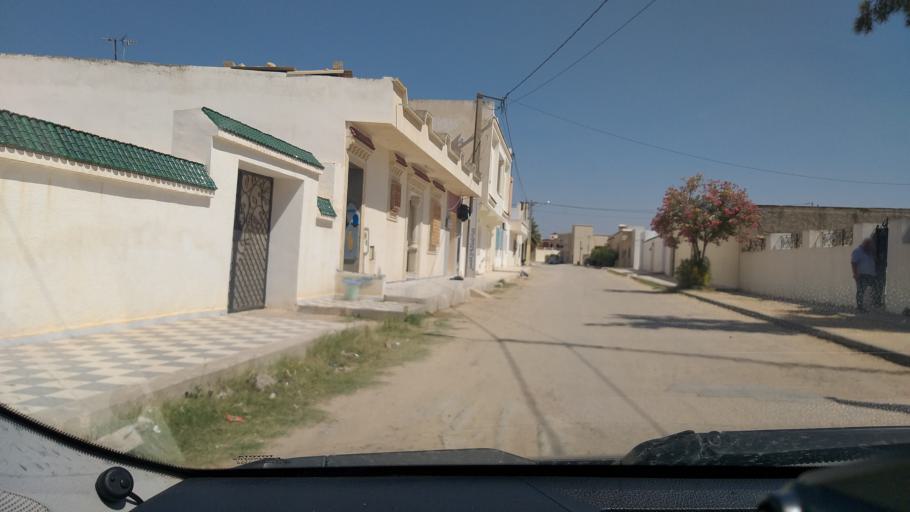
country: TN
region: Al Mahdiyah
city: El Jem
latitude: 35.2899
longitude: 10.7172
